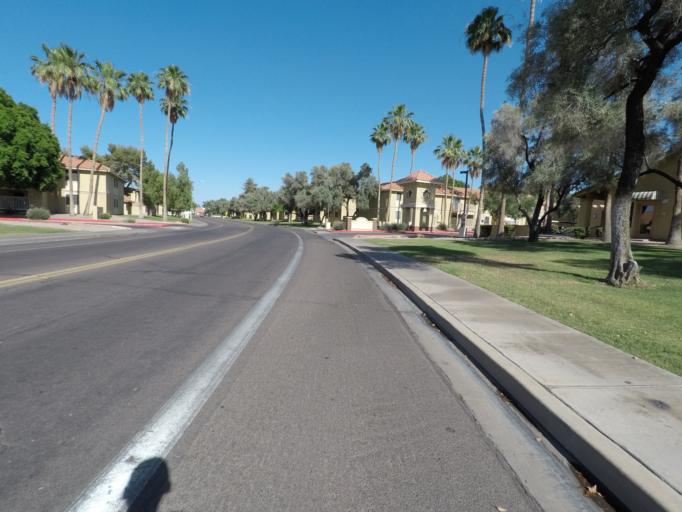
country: US
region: Arizona
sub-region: Maricopa County
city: Tempe
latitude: 33.4096
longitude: -111.9204
